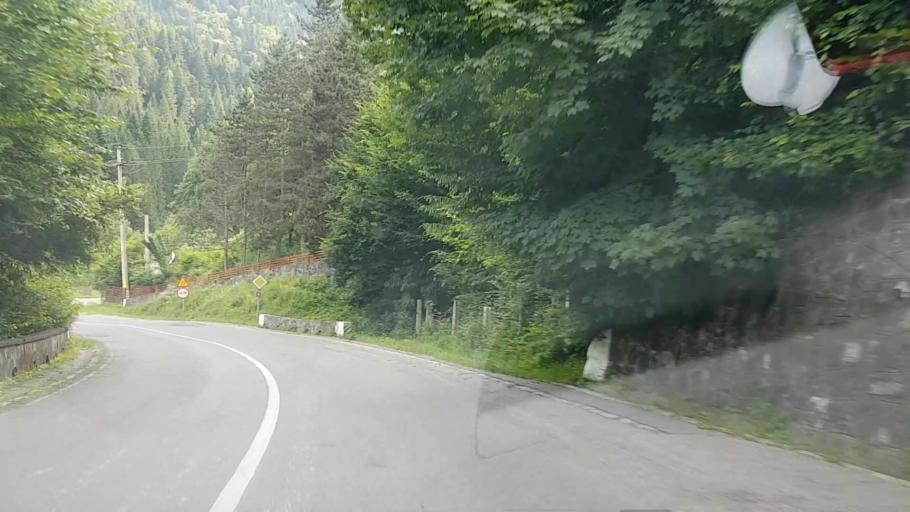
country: RO
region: Neamt
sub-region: Comuna Bicaz
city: Dodeni
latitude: 46.9396
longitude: 26.0836
